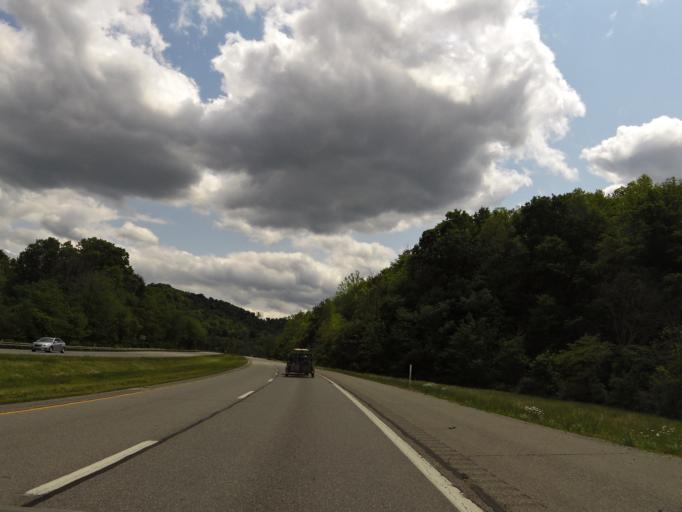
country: US
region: West Virginia
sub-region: Kanawha County
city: Sissonville
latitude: 38.5594
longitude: -81.6364
